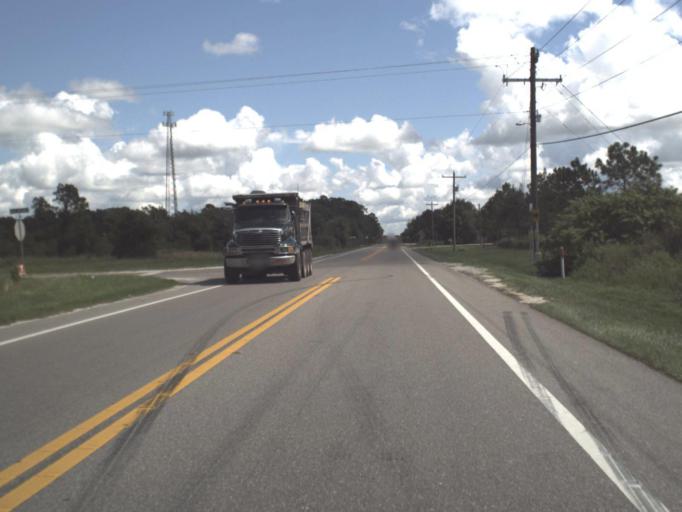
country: US
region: Florida
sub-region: Sarasota County
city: Lake Sarasota
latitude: 27.3871
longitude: -82.2717
